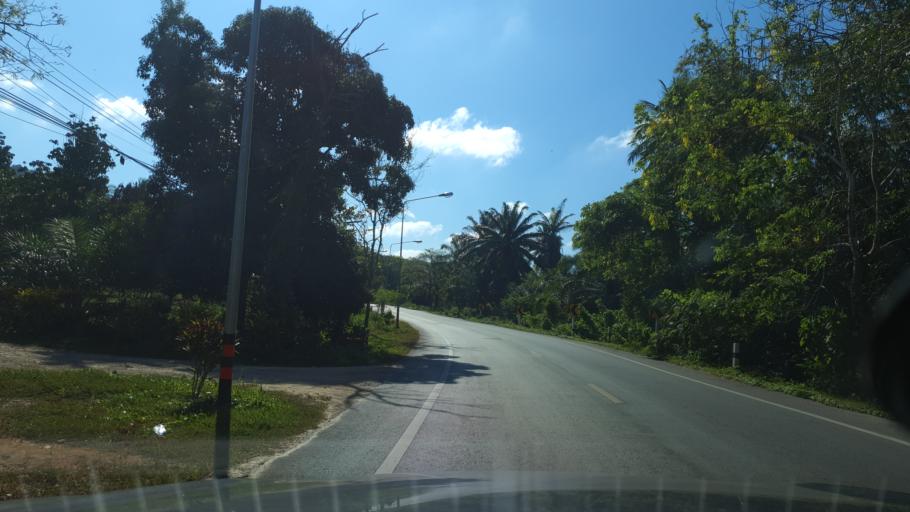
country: TH
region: Phangnga
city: Ban Ao Nang
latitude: 8.0720
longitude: 98.8073
